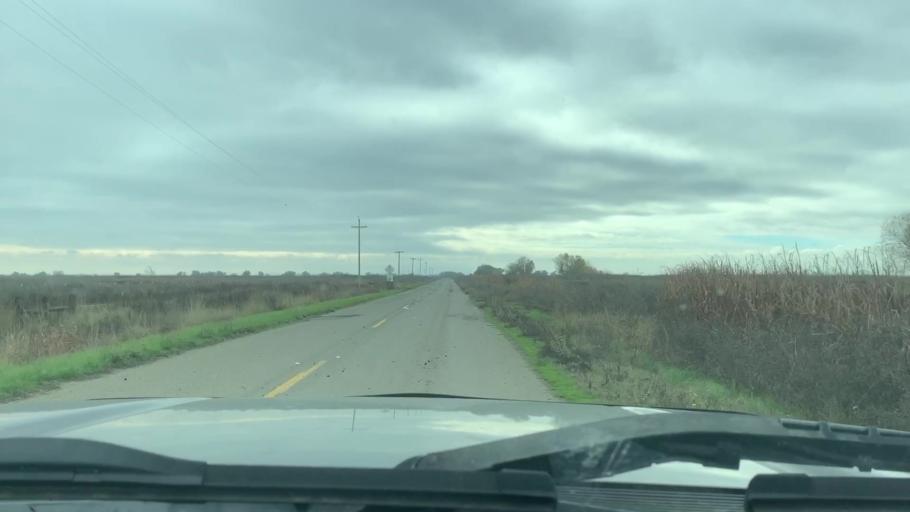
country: US
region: California
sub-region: Merced County
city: Los Banos
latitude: 37.1554
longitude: -120.8155
